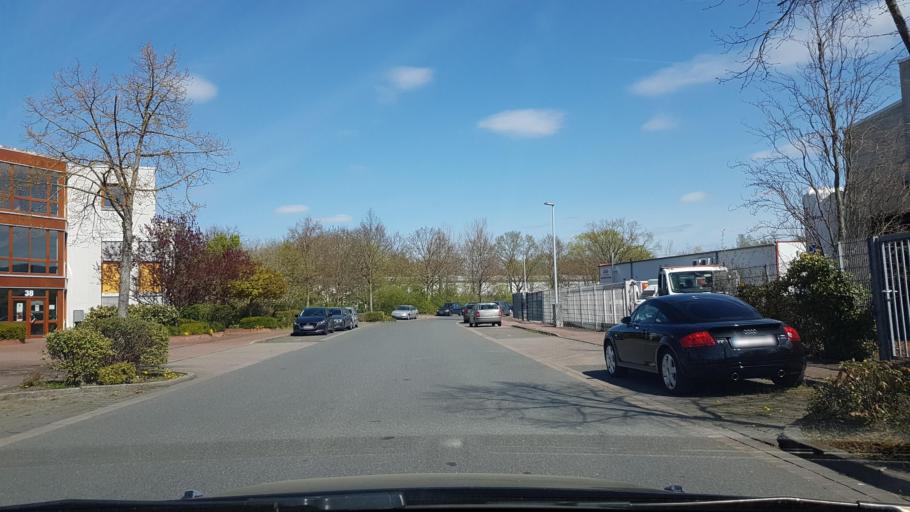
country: DE
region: Lower Saxony
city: Garbsen-Mitte
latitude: 52.4480
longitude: 9.5968
